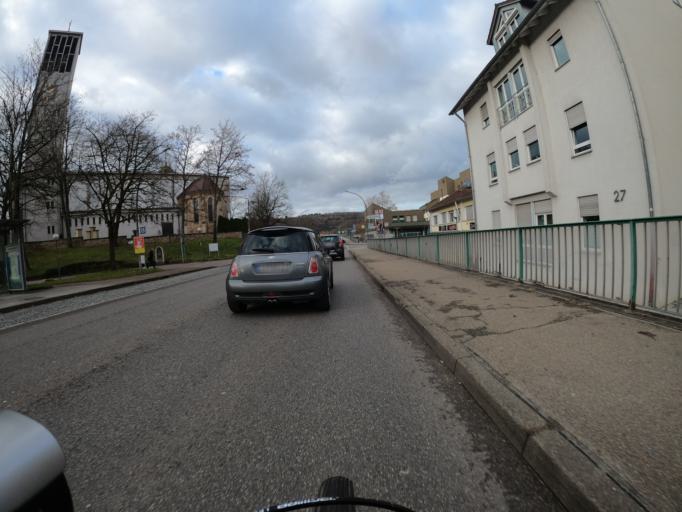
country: DE
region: Baden-Wuerttemberg
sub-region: Regierungsbezirk Stuttgart
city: Wernau
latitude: 48.6932
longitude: 9.4150
